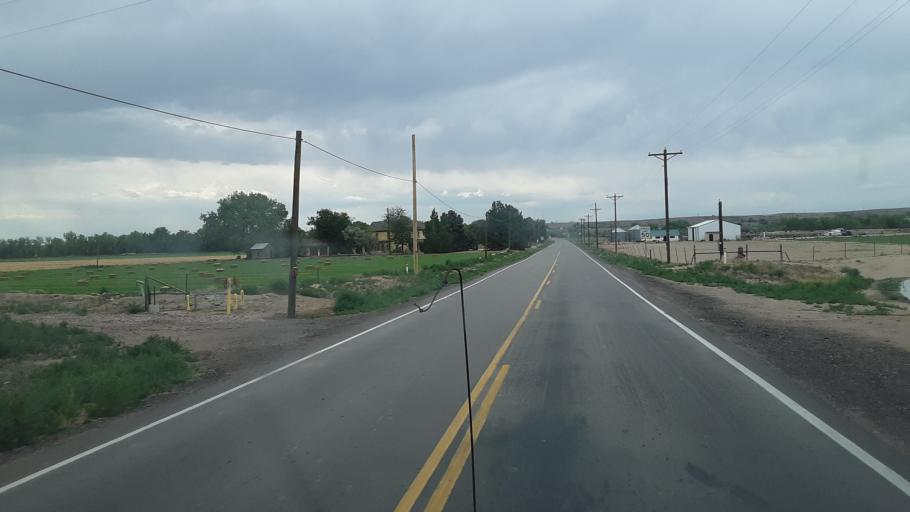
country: US
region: Colorado
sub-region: Otero County
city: Fowler
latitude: 38.1344
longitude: -104.0226
